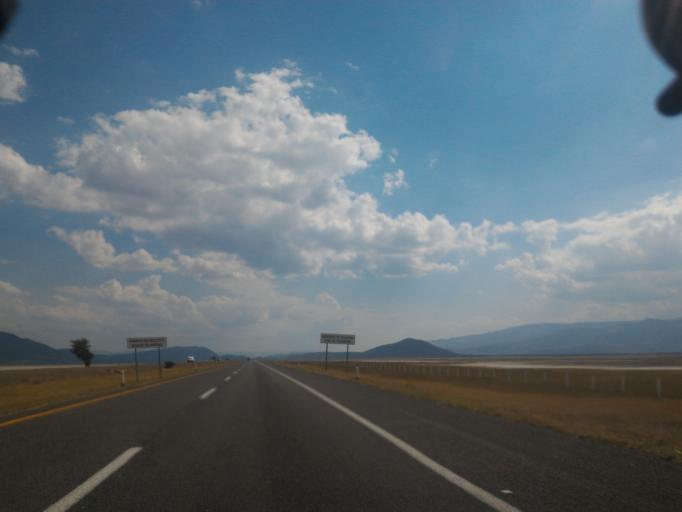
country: MX
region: Jalisco
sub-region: Acatlan de Juarez
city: Villa de los Ninos
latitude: 20.3226
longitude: -103.5663
